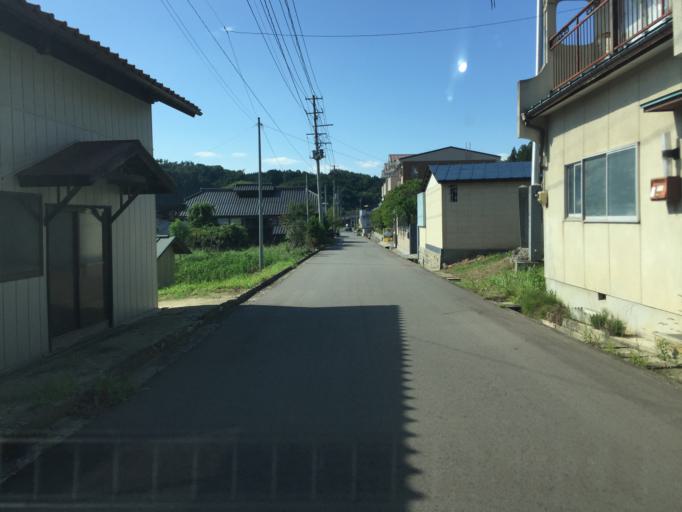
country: JP
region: Fukushima
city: Fukushima-shi
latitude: 37.6735
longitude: 140.5674
